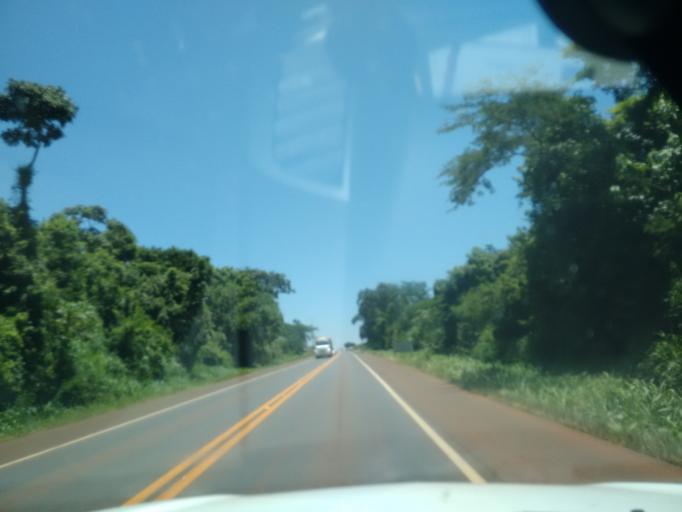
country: BR
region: Parana
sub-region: Marechal Candido Rondon
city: Marechal Candido Rondon
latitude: -24.4520
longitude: -54.1592
